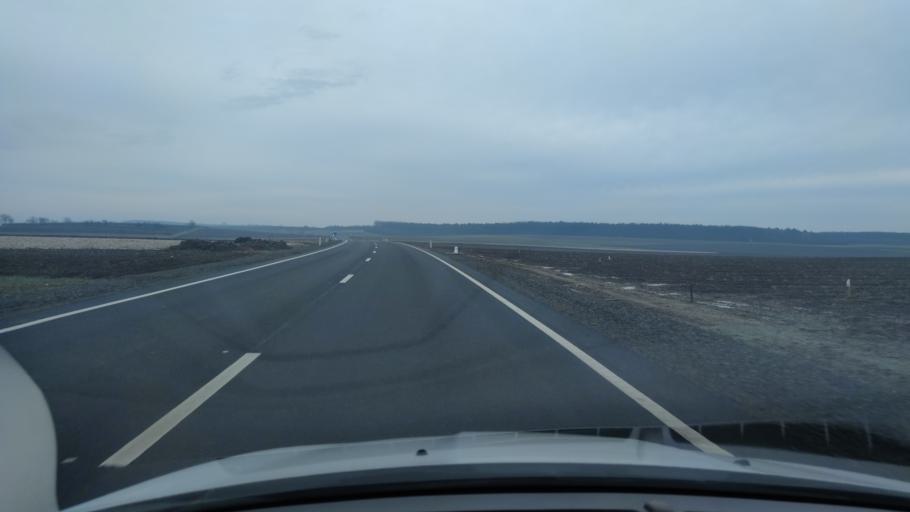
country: RO
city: Szekelyhid
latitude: 47.3351
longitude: 22.1062
